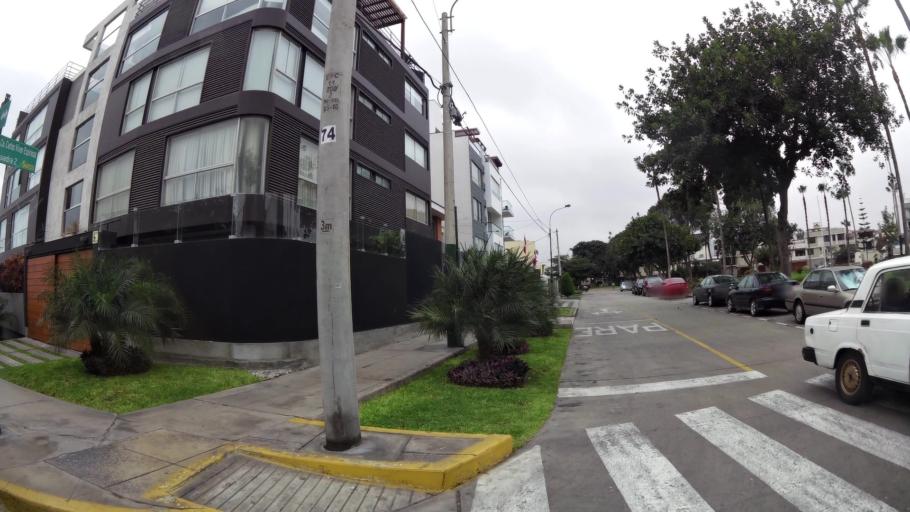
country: PE
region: Lima
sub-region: Lima
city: Surco
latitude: -12.1312
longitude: -77.0146
